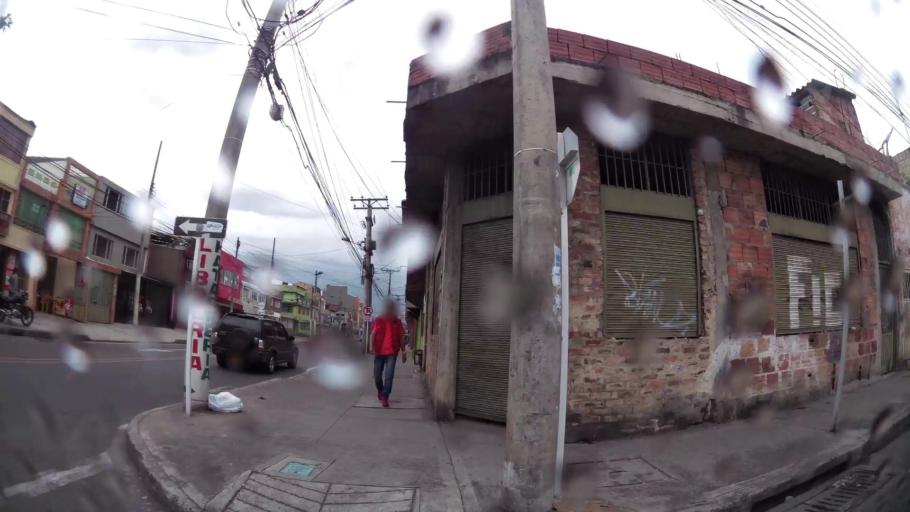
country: CO
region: Bogota D.C.
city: Barrio San Luis
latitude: 4.6952
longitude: -74.0962
